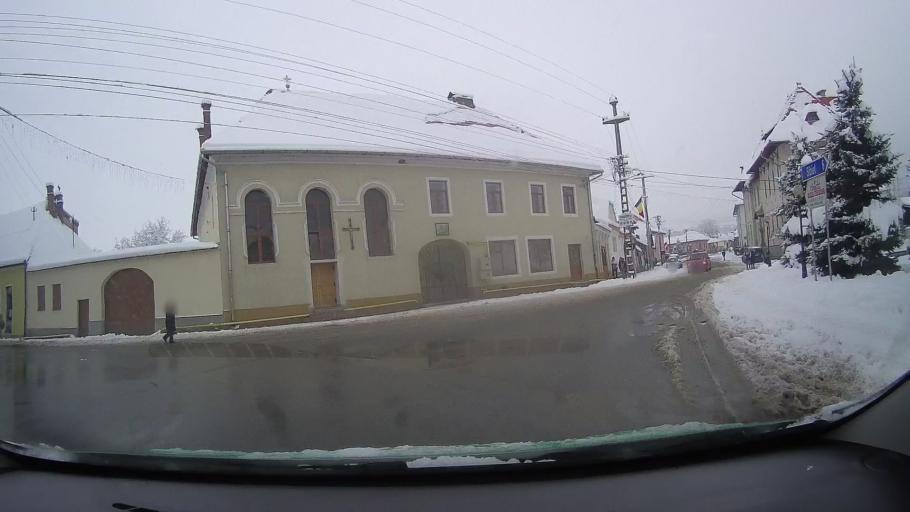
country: RO
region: Sibiu
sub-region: Comuna Orlat
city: Orlat
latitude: 45.7563
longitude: 23.9670
